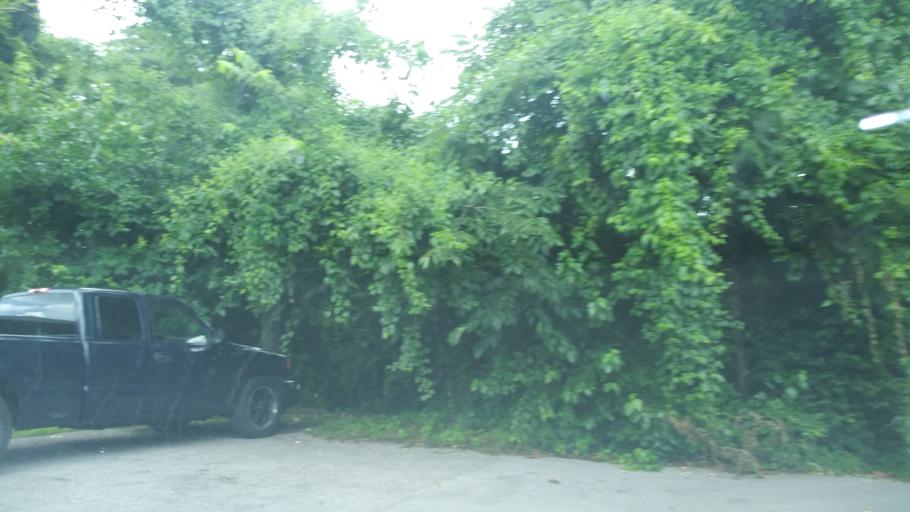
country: US
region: Tennessee
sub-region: Davidson County
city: Nashville
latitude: 36.1328
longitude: -86.7711
